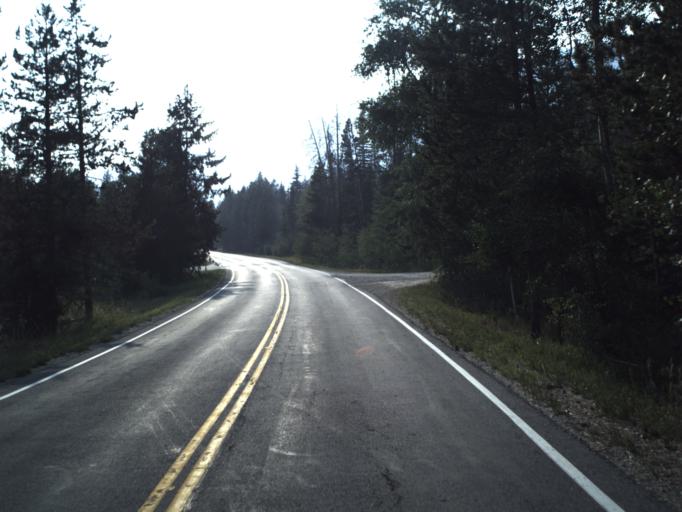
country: US
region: Utah
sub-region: Summit County
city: Francis
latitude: 40.5944
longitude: -110.9963
